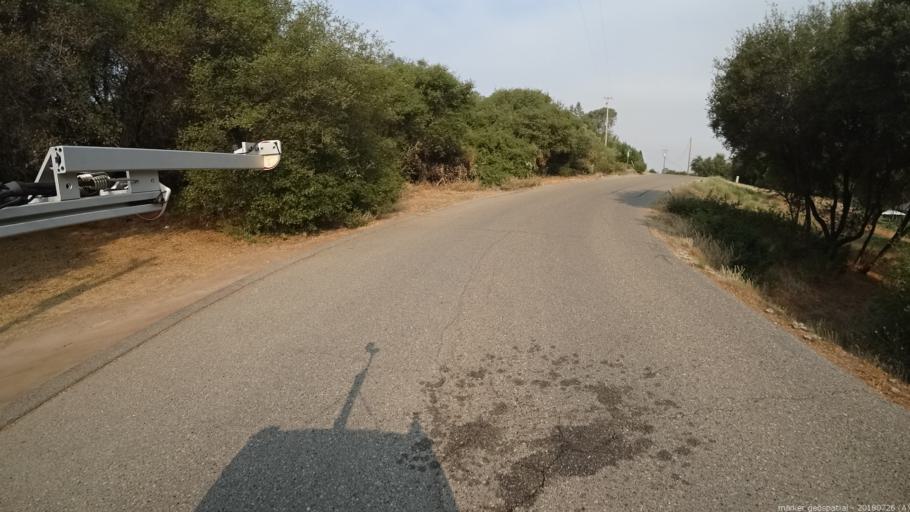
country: US
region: California
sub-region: Madera County
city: Coarsegold
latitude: 37.2014
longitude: -119.6805
